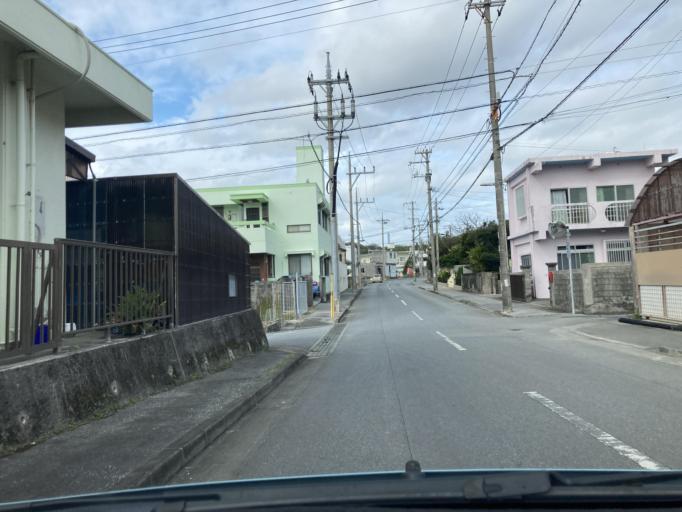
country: JP
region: Okinawa
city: Ginowan
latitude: 26.2057
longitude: 127.7480
